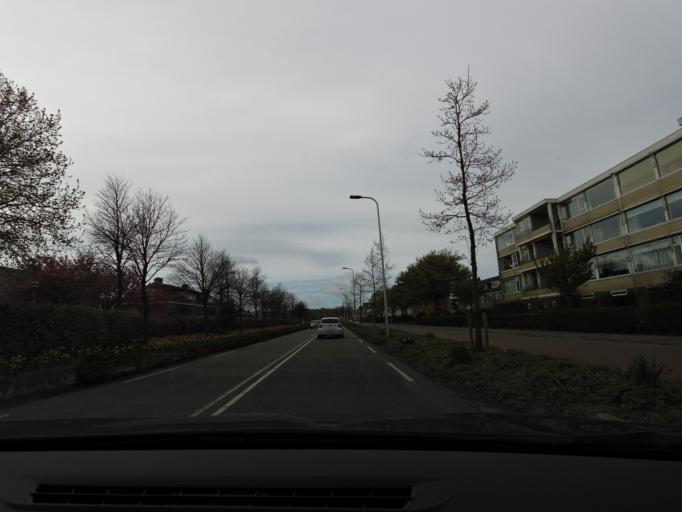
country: NL
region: South Holland
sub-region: Gemeente Noordwijk
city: Noordwijk-Binnen
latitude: 52.2309
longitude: 4.4405
